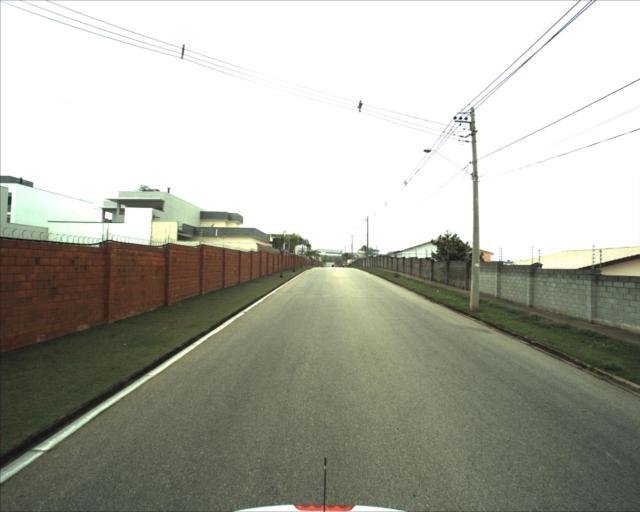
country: BR
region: Sao Paulo
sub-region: Sorocaba
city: Sorocaba
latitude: -23.4450
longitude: -47.4475
